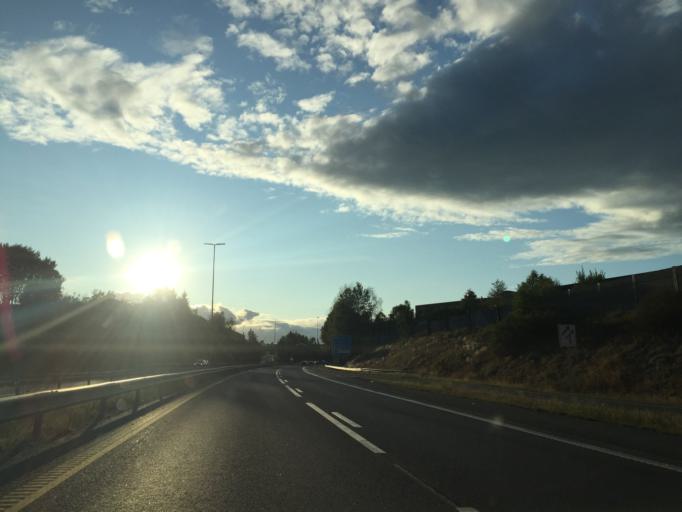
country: NO
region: Akershus
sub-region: Lorenskog
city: Kjenn
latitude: 59.9287
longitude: 10.9542
